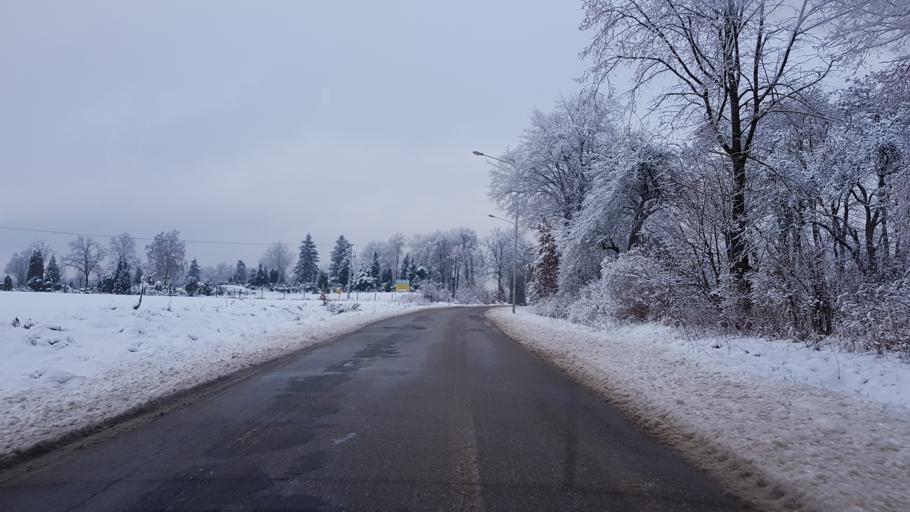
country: PL
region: West Pomeranian Voivodeship
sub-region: Powiat drawski
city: Zlocieniec
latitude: 53.5240
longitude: 16.0073
